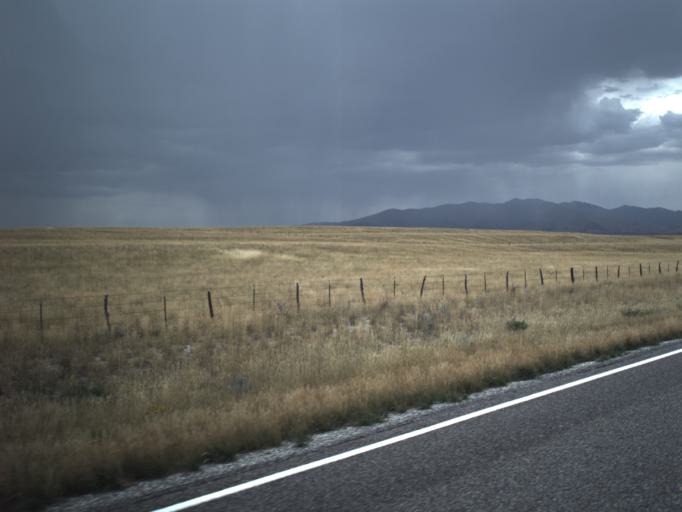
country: US
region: Idaho
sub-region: Oneida County
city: Malad City
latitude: 41.9112
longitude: -113.1005
